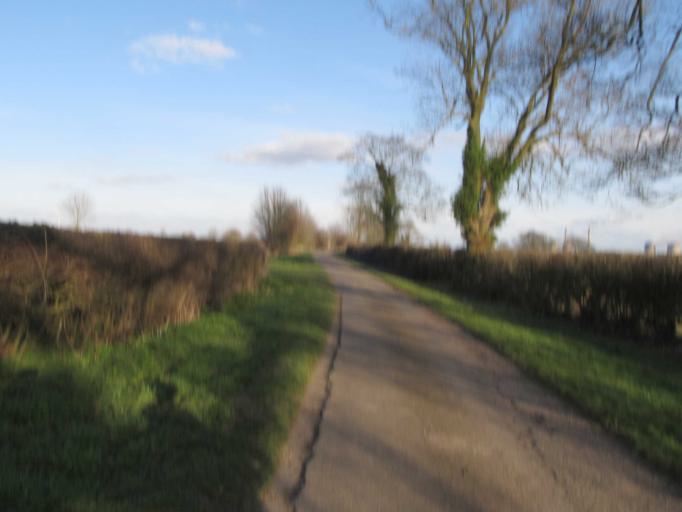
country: GB
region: England
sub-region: Nottinghamshire
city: Misterton
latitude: 53.3779
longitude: -0.8615
